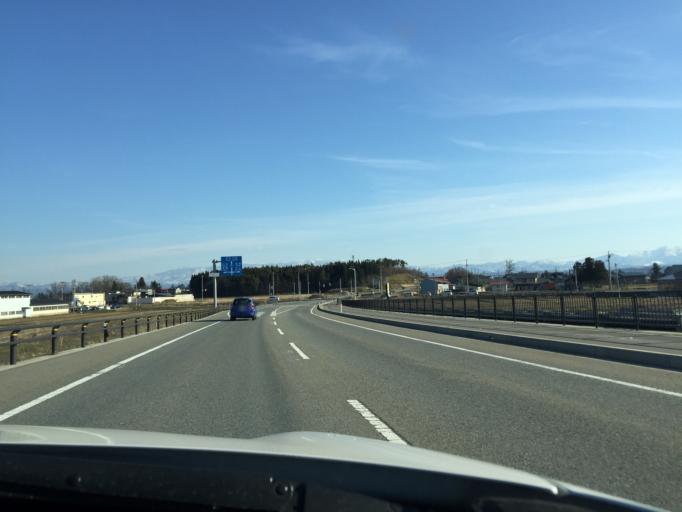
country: JP
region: Yamagata
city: Nagai
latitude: 38.0537
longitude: 140.0613
